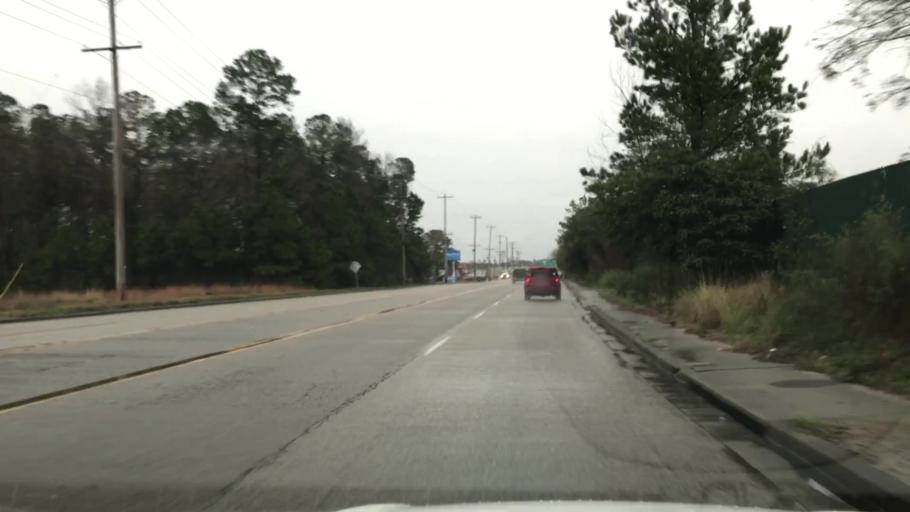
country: US
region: South Carolina
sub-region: Horry County
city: Forestbrook
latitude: 33.7152
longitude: -78.9364
